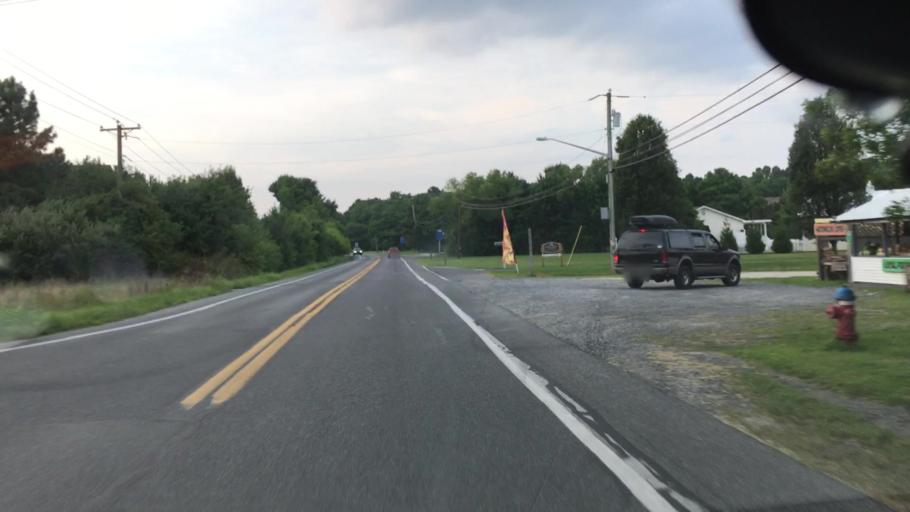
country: US
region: Delaware
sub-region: Sussex County
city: Ocean View
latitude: 38.5337
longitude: -75.0889
